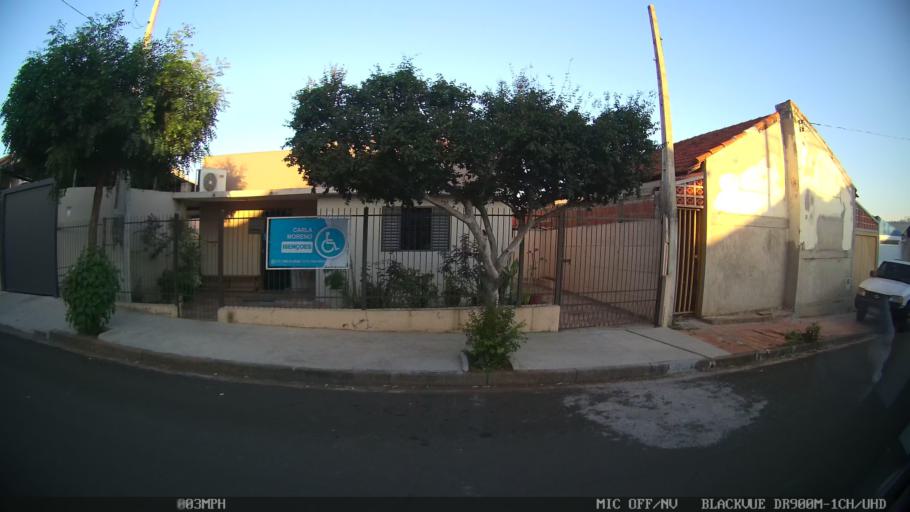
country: BR
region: Sao Paulo
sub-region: Sao Jose Do Rio Preto
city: Sao Jose do Rio Preto
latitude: -20.8030
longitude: -49.3678
